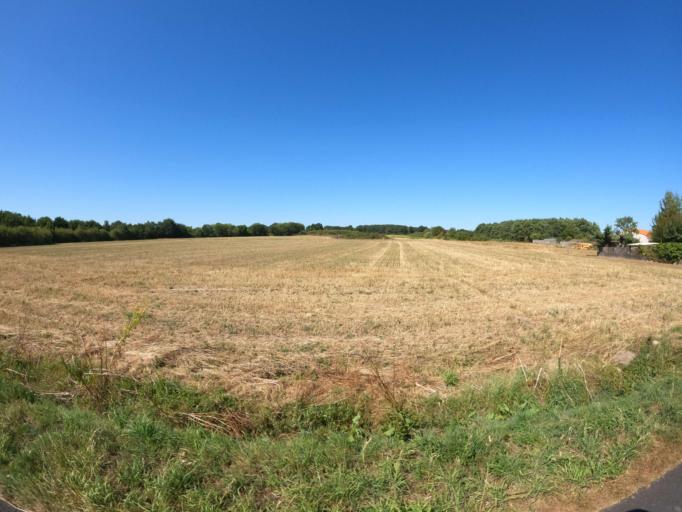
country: FR
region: Pays de la Loire
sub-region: Departement de la Vendee
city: La Guyonniere
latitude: 46.9637
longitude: -1.2693
